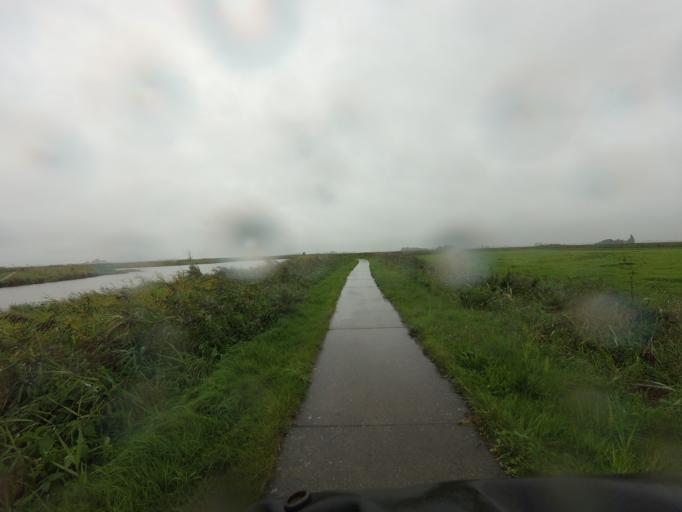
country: NL
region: Friesland
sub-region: Sudwest Fryslan
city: Workum
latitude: 52.9984
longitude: 5.5136
